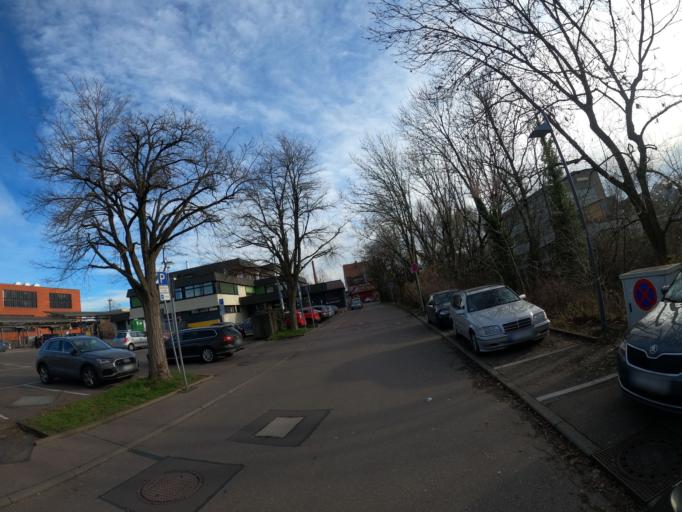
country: DE
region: Baden-Wuerttemberg
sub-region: Regierungsbezirk Stuttgart
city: Eislingen
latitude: 48.6962
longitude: 9.7045
